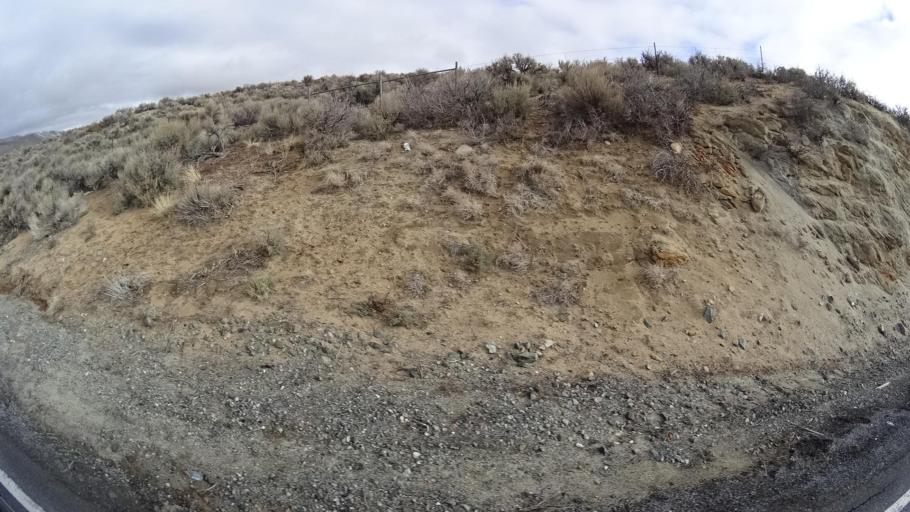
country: US
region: Nevada
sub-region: Washoe County
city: Cold Springs
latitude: 39.8035
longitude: -119.9179
